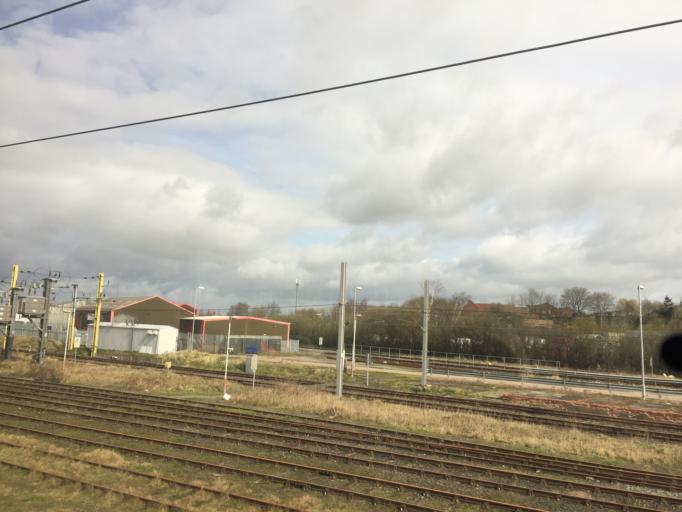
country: GB
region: England
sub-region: Cumbria
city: Carlisle
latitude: 54.8831
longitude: -2.9233
